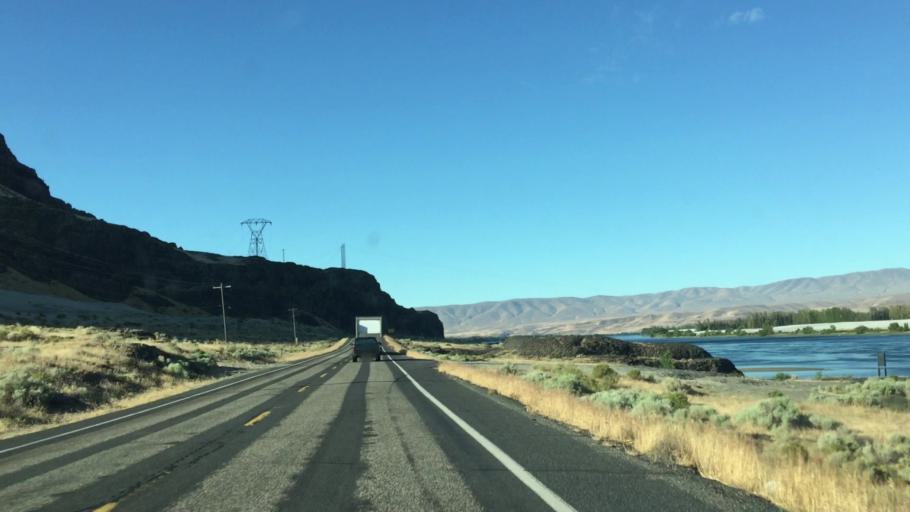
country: US
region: Washington
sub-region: Grant County
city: Mattawa
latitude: 46.8063
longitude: -119.9218
